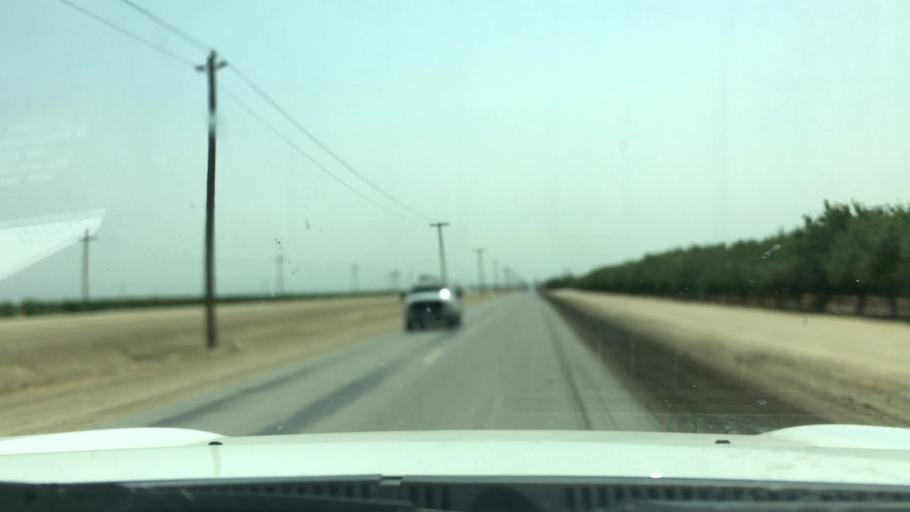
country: US
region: California
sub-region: Kern County
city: Wasco
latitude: 35.6268
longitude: -119.4378
